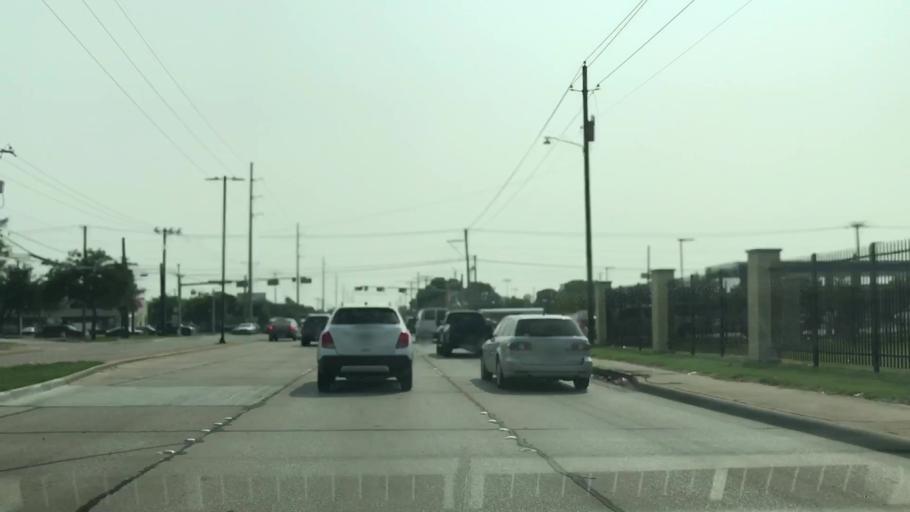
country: US
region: Texas
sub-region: Dallas County
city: Garland
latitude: 32.8796
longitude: -96.6206
